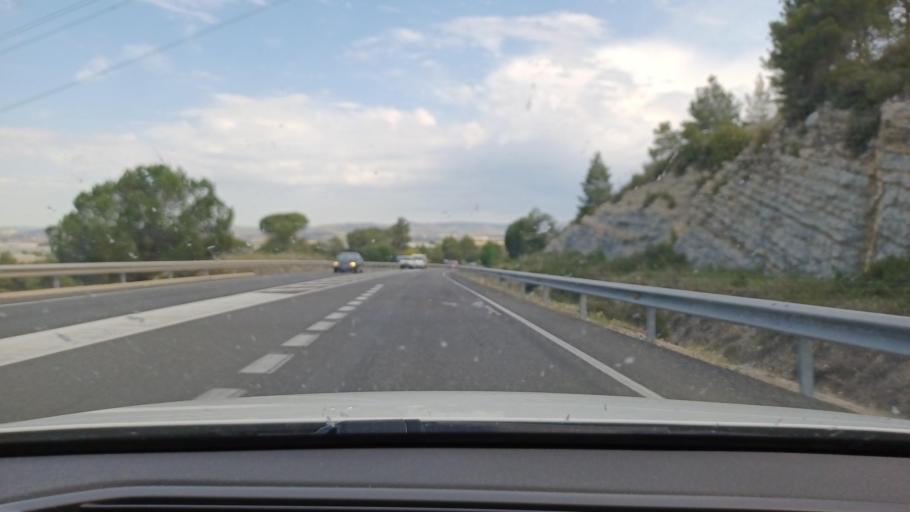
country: ES
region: Catalonia
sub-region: Provincia de Barcelona
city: La Pobla de Claramunt
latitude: 41.5655
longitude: 1.6773
